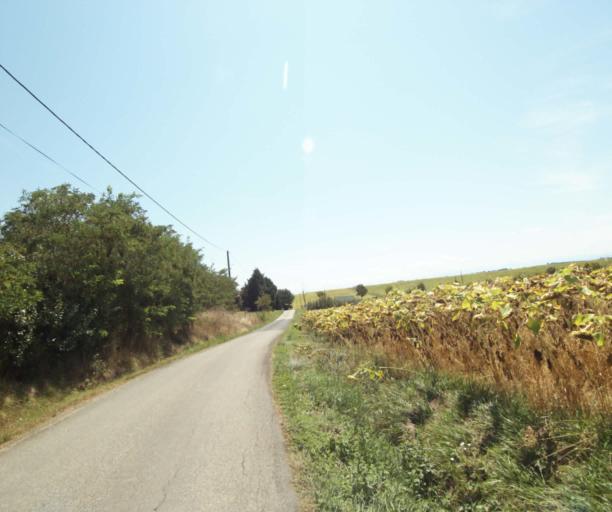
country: FR
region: Midi-Pyrenees
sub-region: Departement de l'Ariege
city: Lezat-sur-Leze
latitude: 43.2869
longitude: 1.3026
